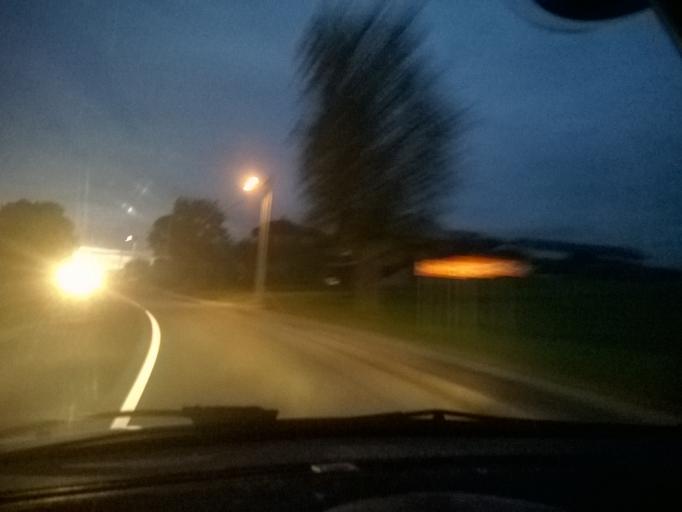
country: HR
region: Krapinsko-Zagorska
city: Zabok
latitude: 46.0719
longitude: 15.9228
